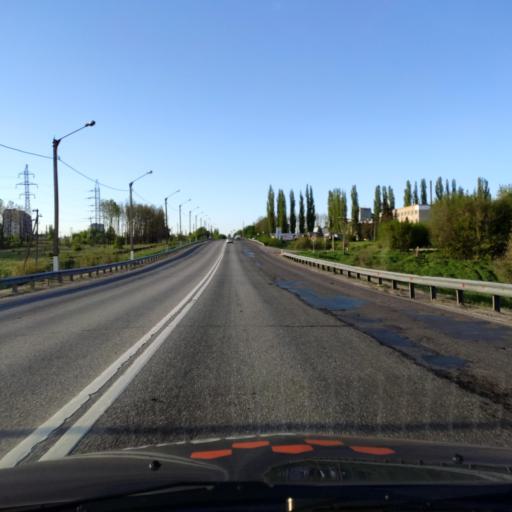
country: RU
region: Lipetsk
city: Yelets
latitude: 52.6158
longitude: 38.4608
